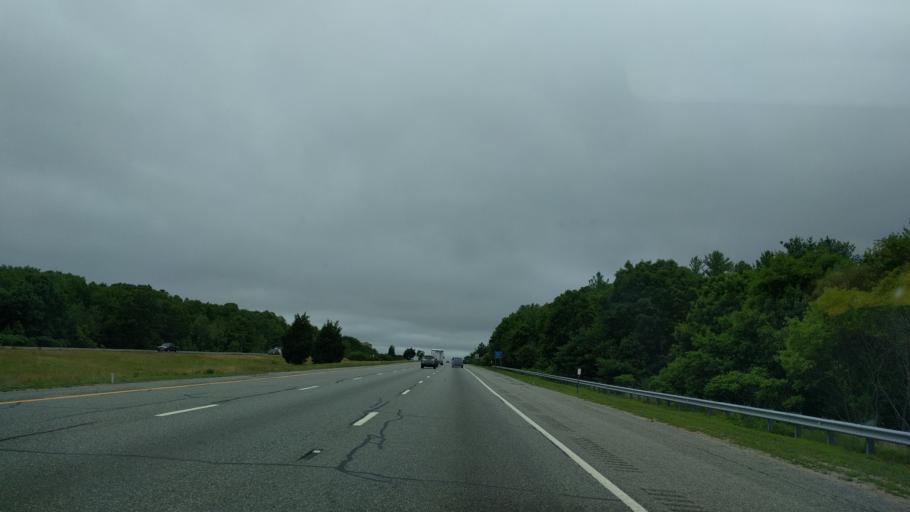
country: US
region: Rhode Island
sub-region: Providence County
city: Cumberland Hill
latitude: 41.9407
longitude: -71.4865
